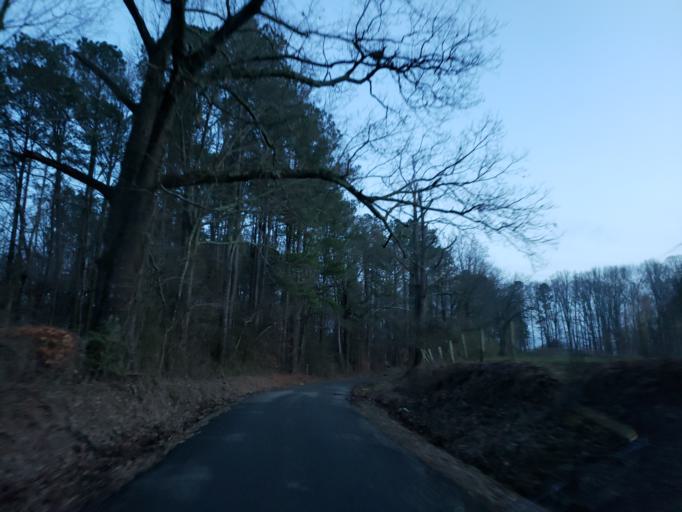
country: US
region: Georgia
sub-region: Cherokee County
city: Ball Ground
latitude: 34.2906
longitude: -84.2812
